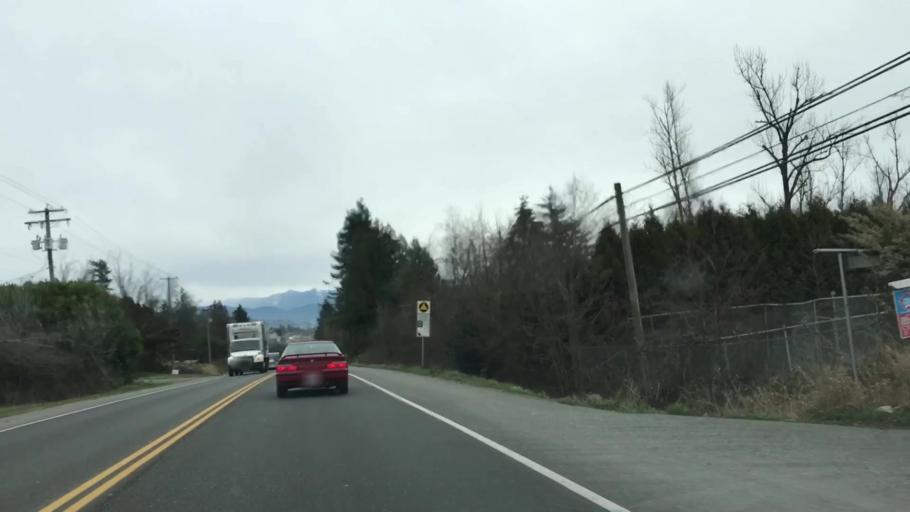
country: CA
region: British Columbia
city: Aldergrove
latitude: 49.0571
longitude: -122.3965
